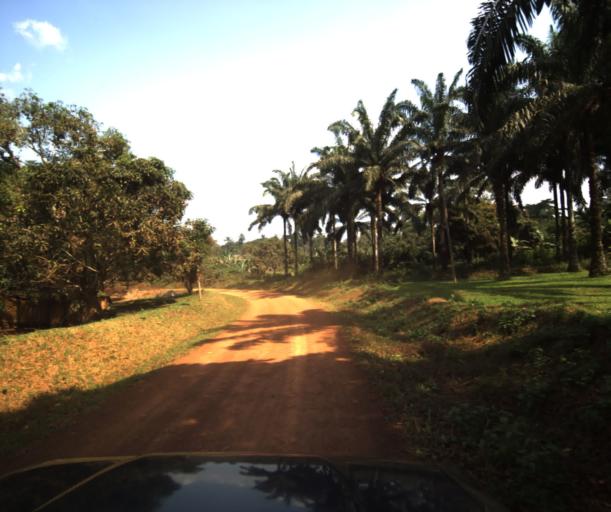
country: CM
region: Centre
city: Akono
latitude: 3.6023
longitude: 11.2314
